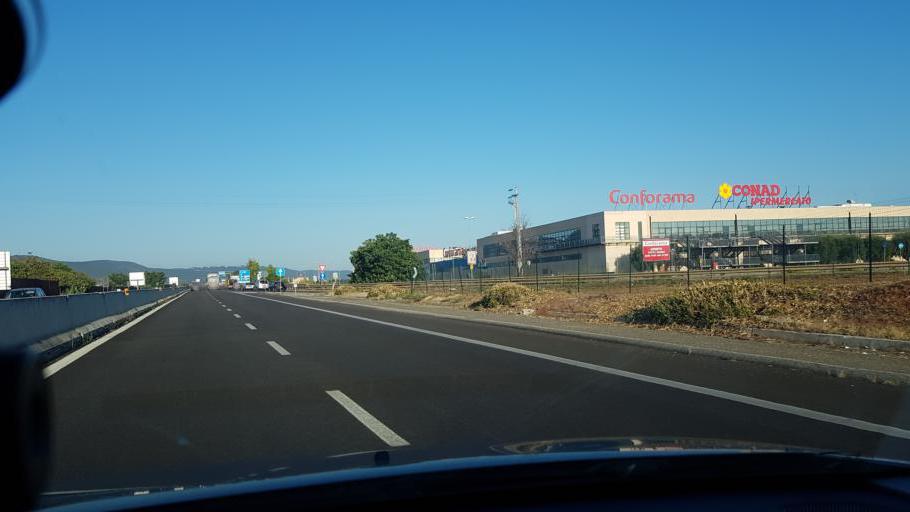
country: IT
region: Apulia
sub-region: Provincia di Brindisi
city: Fasano
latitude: 40.8378
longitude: 17.3810
